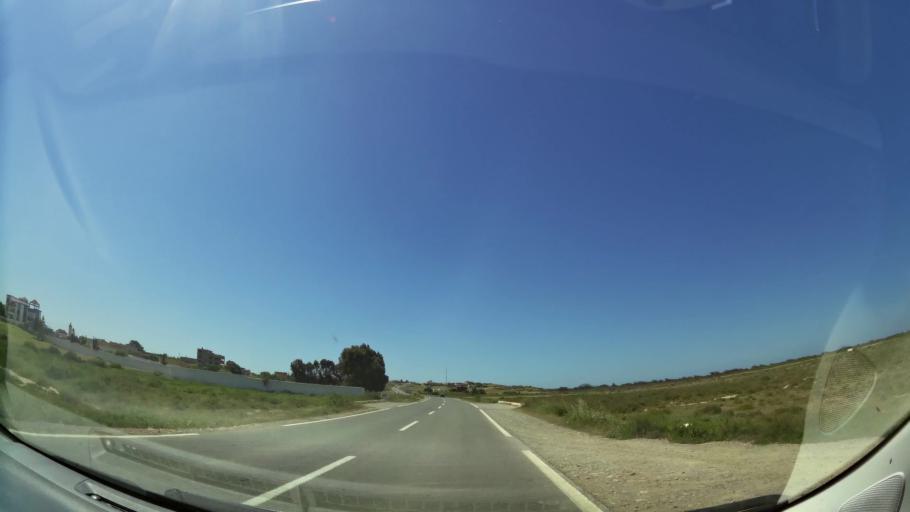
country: MA
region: Oriental
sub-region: Berkane-Taourirt
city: Madagh
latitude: 35.1186
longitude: -2.3727
